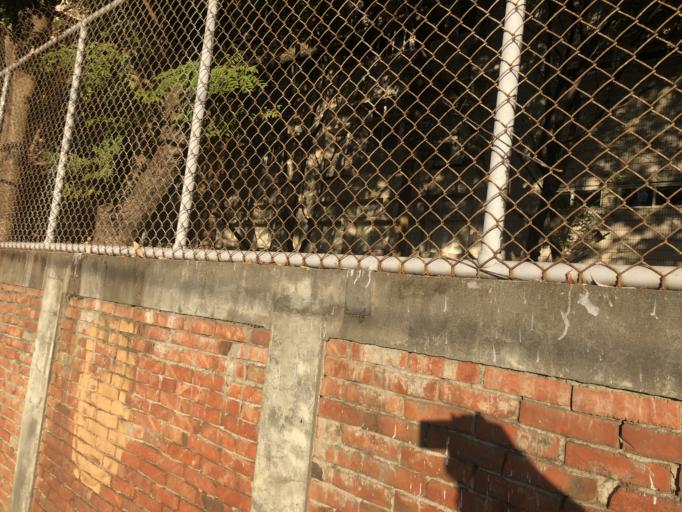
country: TW
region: Taiwan
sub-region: Taichung City
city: Taichung
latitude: 24.1378
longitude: 120.6071
